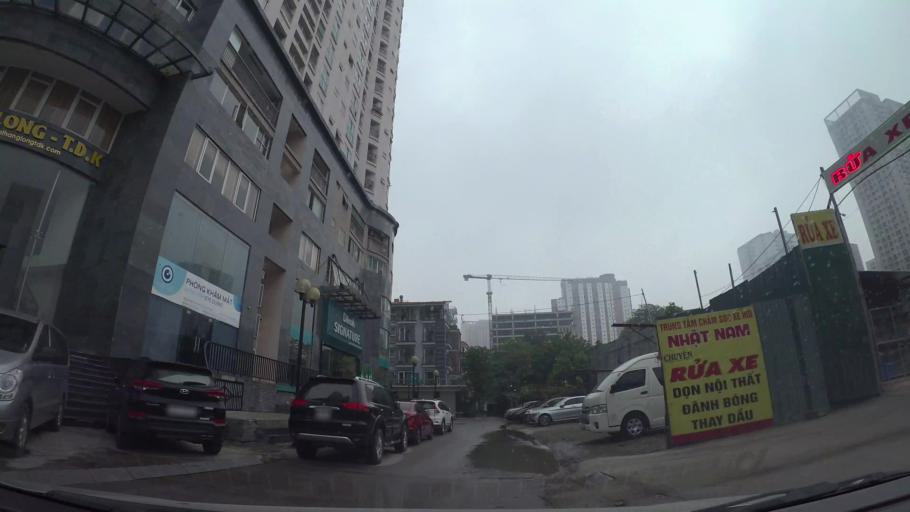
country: VN
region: Ha Noi
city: Cau Giay
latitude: 21.0207
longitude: 105.7898
